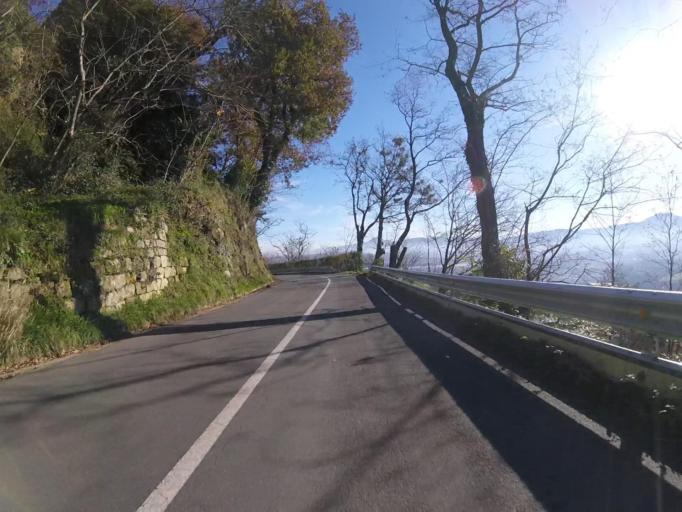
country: ES
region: Basque Country
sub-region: Provincia de Guipuzcoa
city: Fuenterrabia
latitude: 43.3691
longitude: -1.8125
